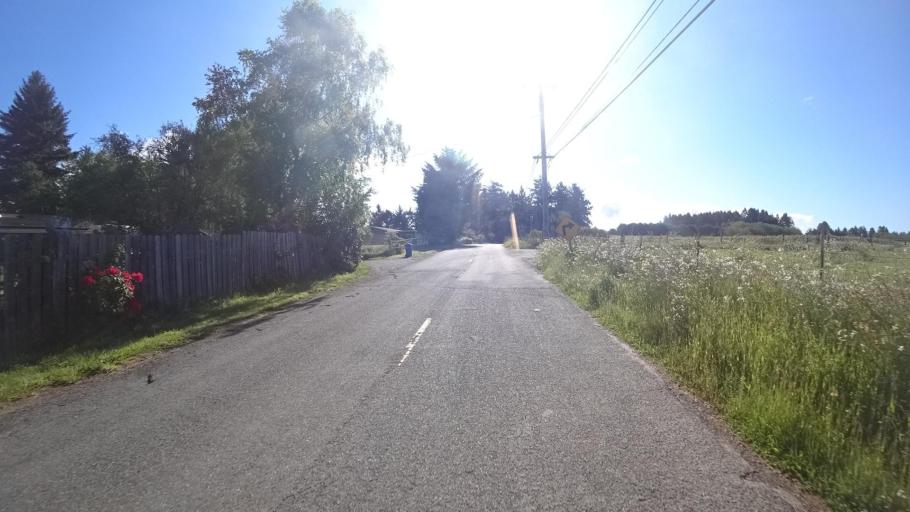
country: US
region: California
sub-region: Humboldt County
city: Westhaven-Moonstone
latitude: 41.0051
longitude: -124.1031
